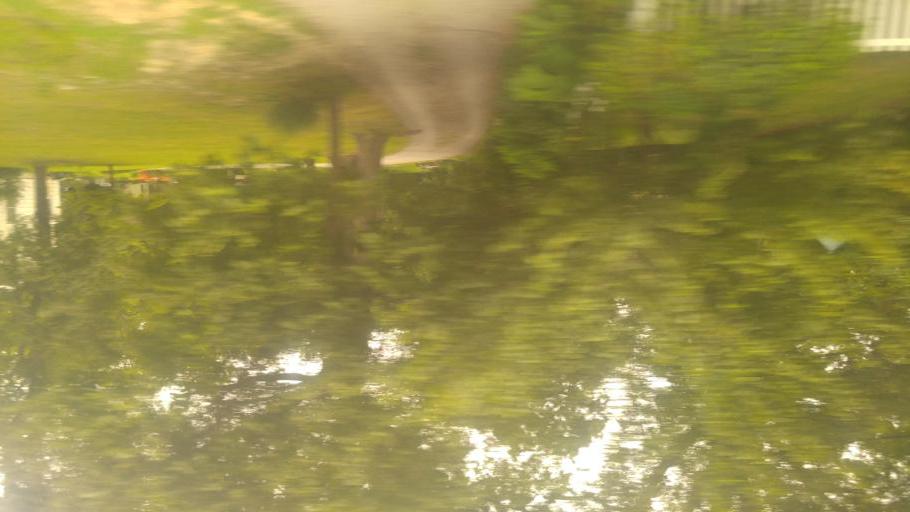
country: US
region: Virginia
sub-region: Hanover County
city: Ashland
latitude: 37.7497
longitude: -77.4842
